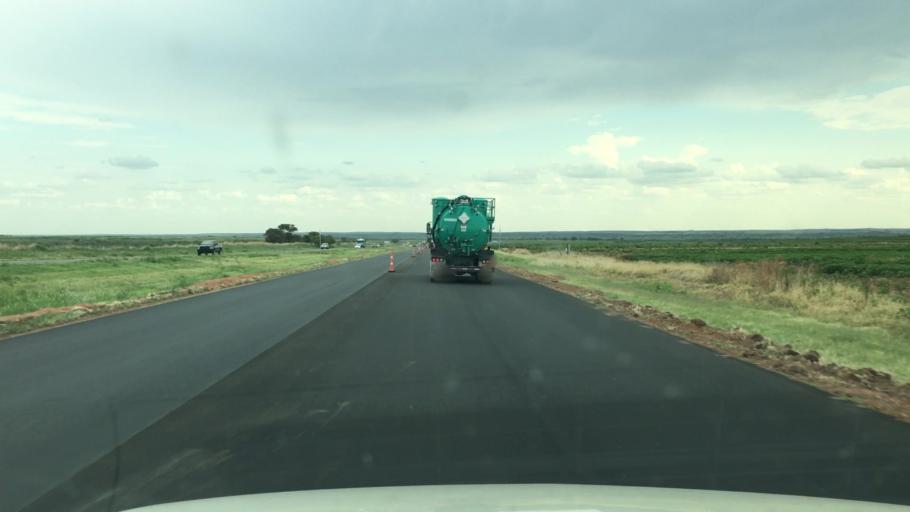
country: US
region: Texas
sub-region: Hall County
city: Memphis
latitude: 34.6117
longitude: -100.4691
